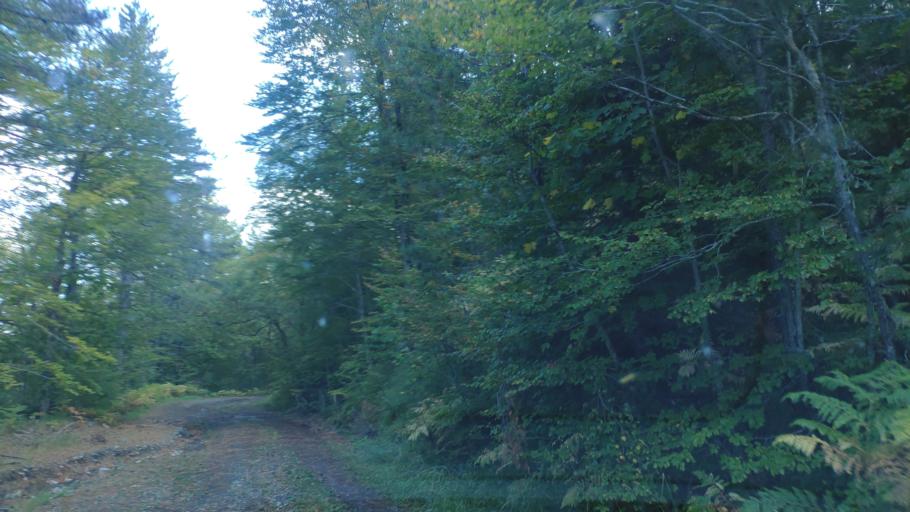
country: AL
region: Korce
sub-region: Rrethi i Devollit
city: Miras
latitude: 40.3469
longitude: 20.8991
